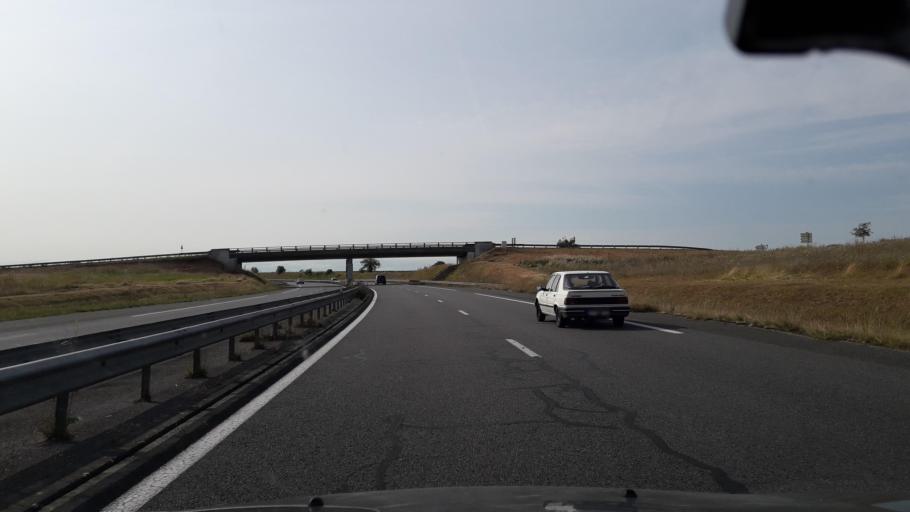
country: FR
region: Poitou-Charentes
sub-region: Departement de la Charente
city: Saint-Meme-les-Carrieres
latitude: 45.6906
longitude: -0.0855
